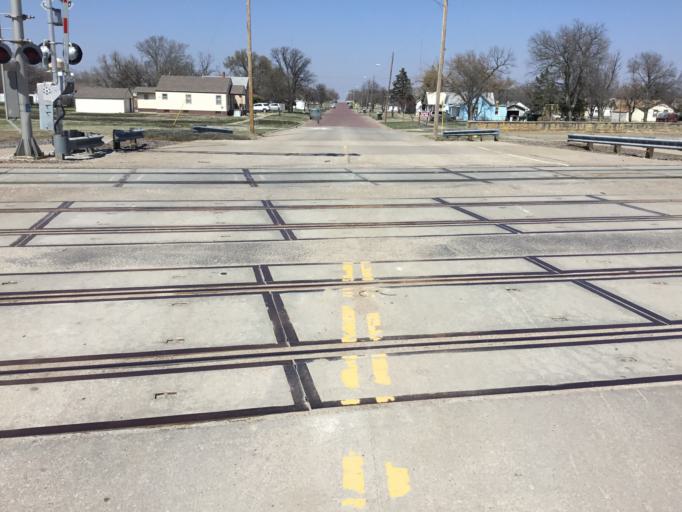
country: US
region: Kansas
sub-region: Russell County
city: Russell
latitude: 38.8945
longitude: -98.8599
